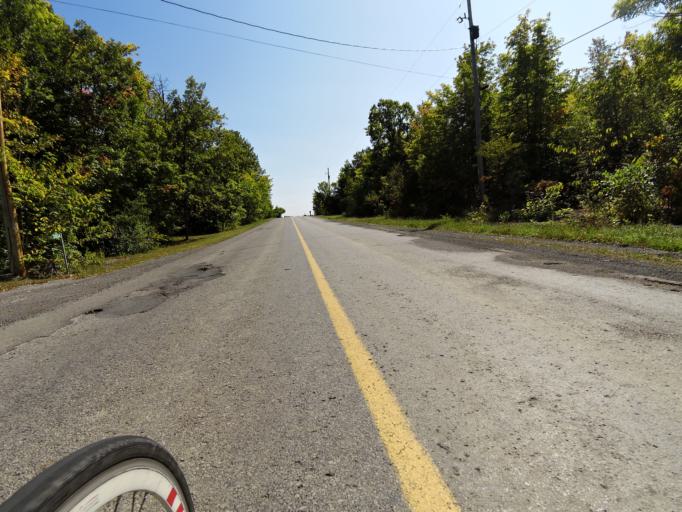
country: CA
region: Ontario
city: Bells Corners
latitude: 45.4159
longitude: -76.0378
